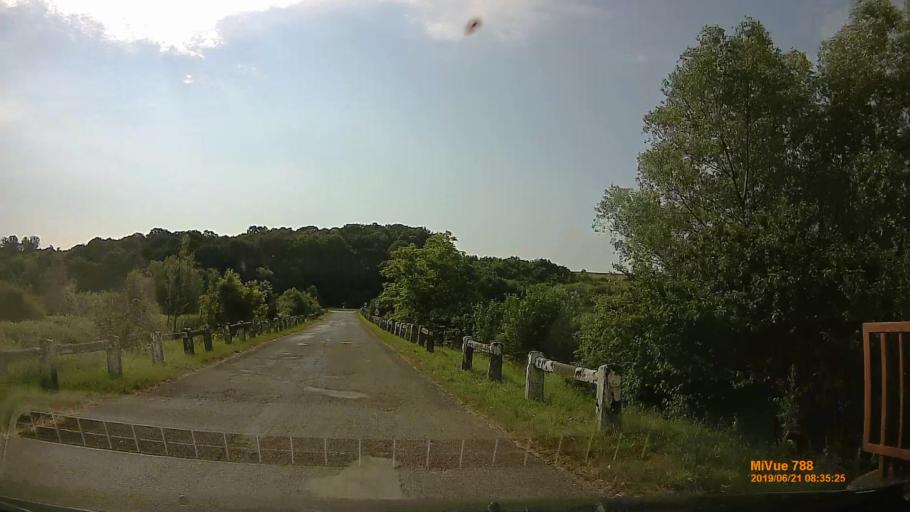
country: HU
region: Baranya
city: Buekkoesd
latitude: 46.1691
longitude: 17.8967
